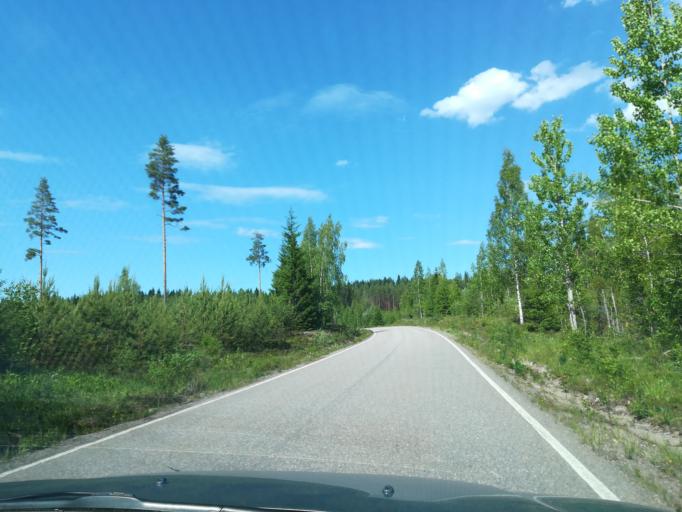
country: FI
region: South Karelia
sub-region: Imatra
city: Ruokolahti
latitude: 61.4775
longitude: 28.8731
